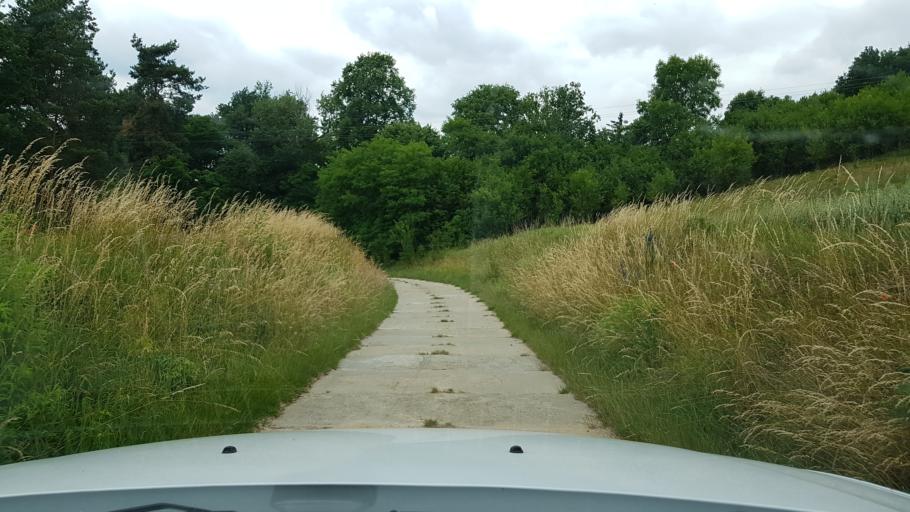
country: PL
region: West Pomeranian Voivodeship
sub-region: Powiat mysliborski
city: Boleszkowice
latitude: 52.6770
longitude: 14.6234
